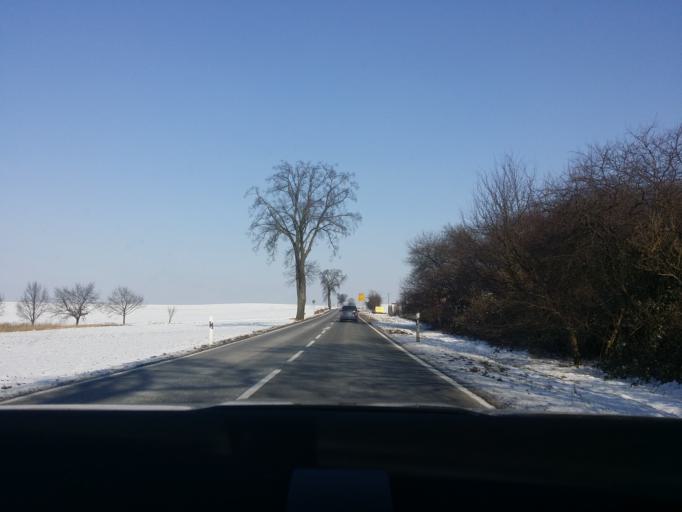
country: DE
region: Mecklenburg-Vorpommern
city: Penzlin
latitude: 53.5206
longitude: 13.1246
